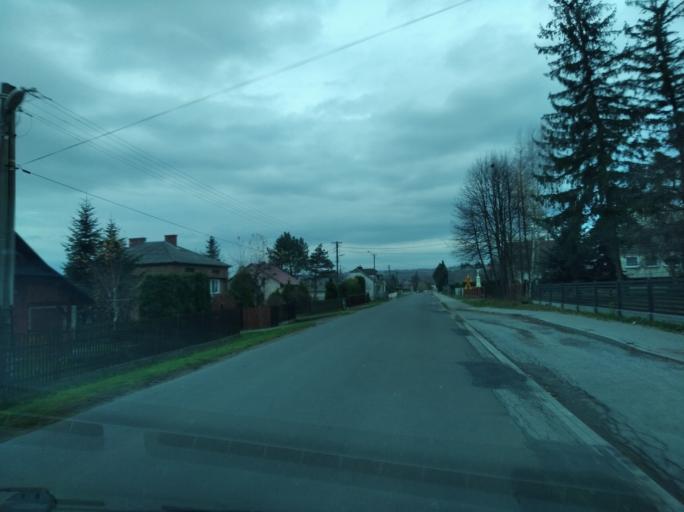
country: PL
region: Subcarpathian Voivodeship
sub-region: Powiat ropczycko-sedziszowski
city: Iwierzyce
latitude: 50.0138
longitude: 21.7526
